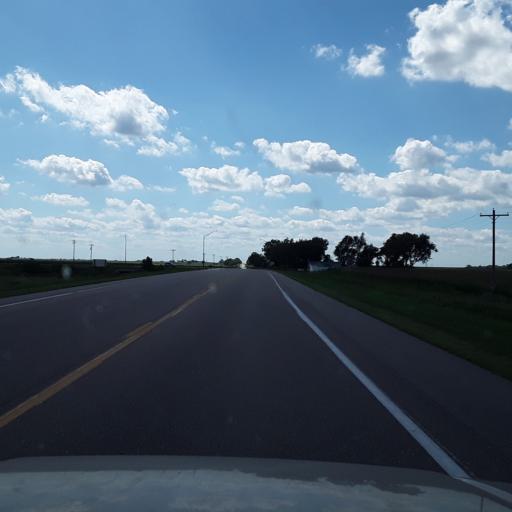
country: US
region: Nebraska
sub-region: Merrick County
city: Central City
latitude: 41.1911
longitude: -97.9991
